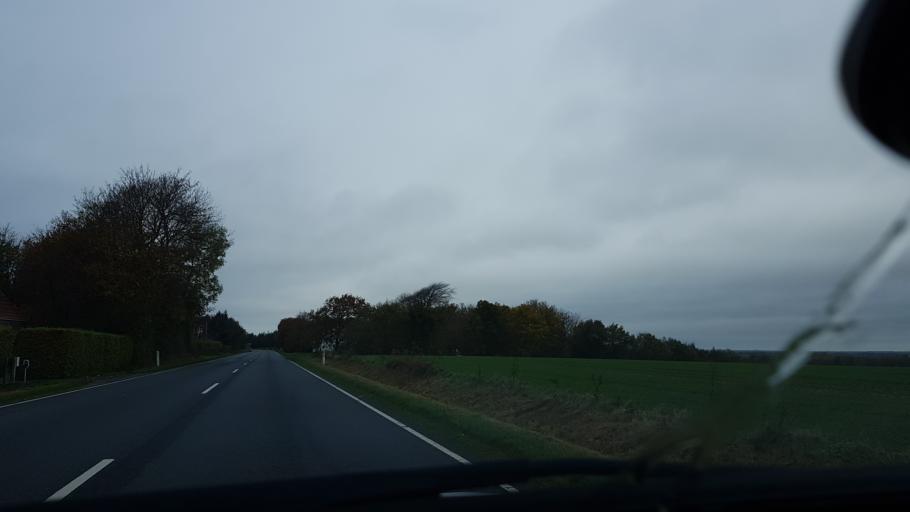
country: DK
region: South Denmark
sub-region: Esbjerg Kommune
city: Ribe
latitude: 55.2767
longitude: 8.8622
